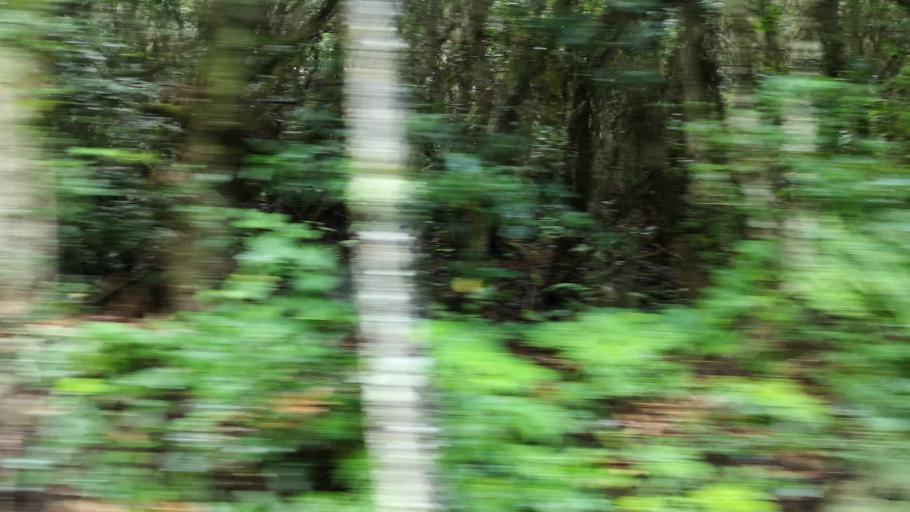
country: ES
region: Canary Islands
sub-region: Provincia de Santa Cruz de Tenerife
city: Vallehermosa
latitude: 28.1630
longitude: -17.2962
